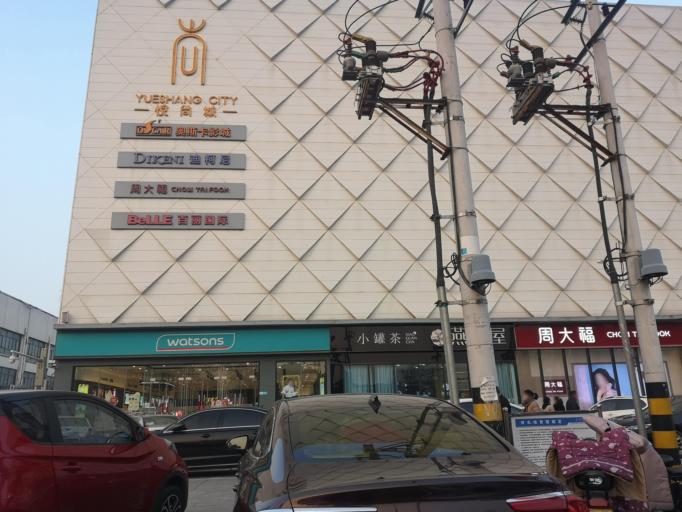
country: CN
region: Henan Sheng
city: Zhongyuanlu
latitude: 35.7712
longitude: 115.0558
